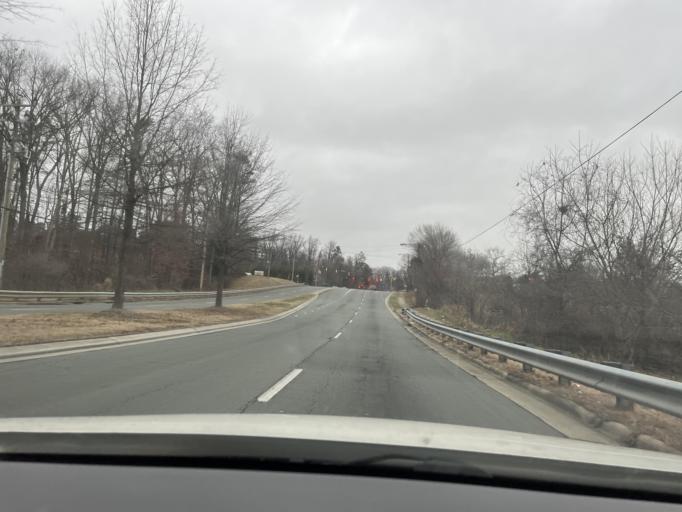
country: US
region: North Carolina
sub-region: Guilford County
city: Greensboro
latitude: 36.0133
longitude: -79.7936
